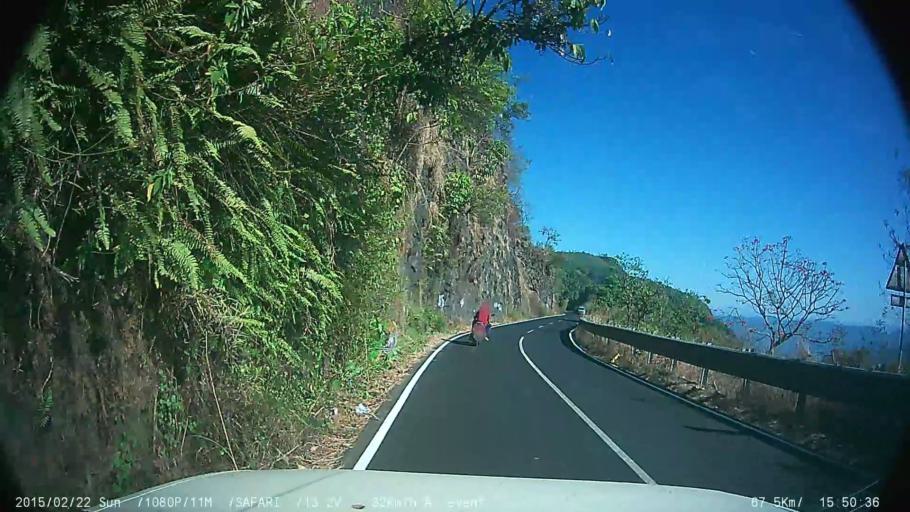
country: IN
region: Kerala
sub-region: Kottayam
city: Erattupetta
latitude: 9.5701
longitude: 77.0037
